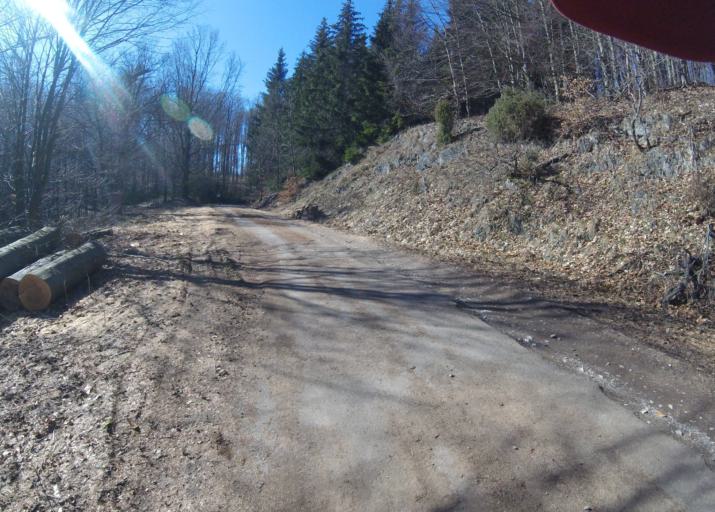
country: HU
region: Heves
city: Szilvasvarad
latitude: 48.0712
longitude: 20.4669
